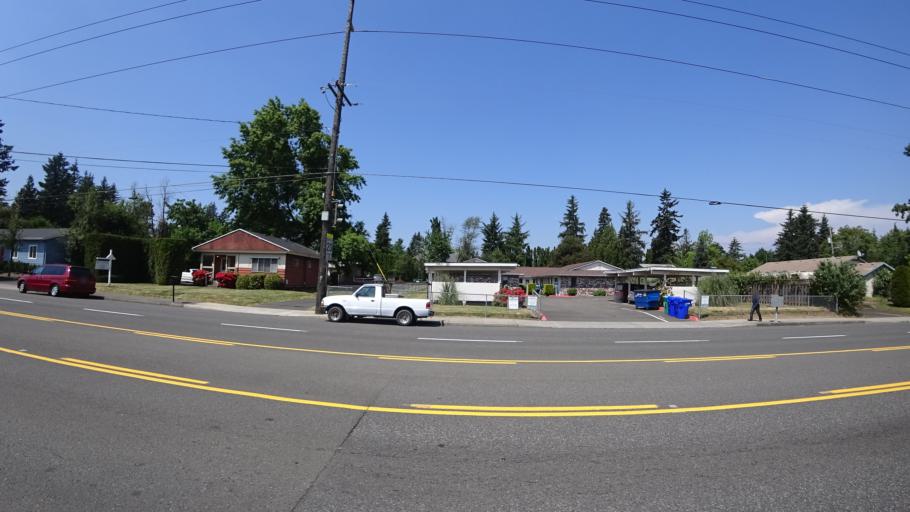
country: US
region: Oregon
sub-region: Multnomah County
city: Fairview
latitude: 45.5264
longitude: -122.5024
